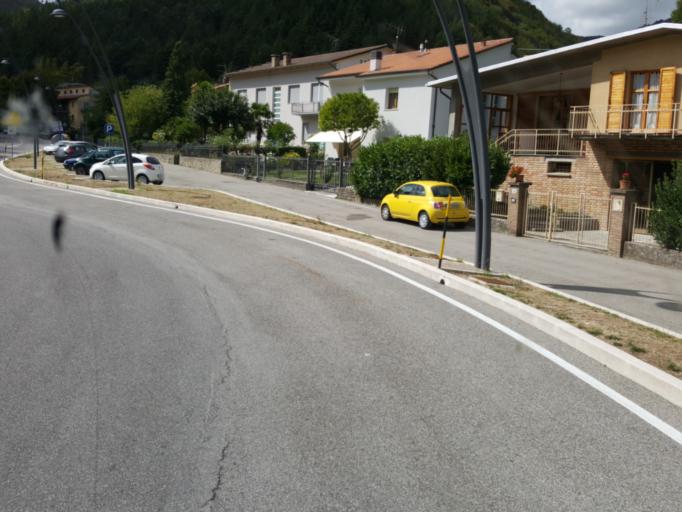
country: IT
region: Emilia-Romagna
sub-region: Forli-Cesena
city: San Piero in Bagno
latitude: 43.8375
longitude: 11.9618
